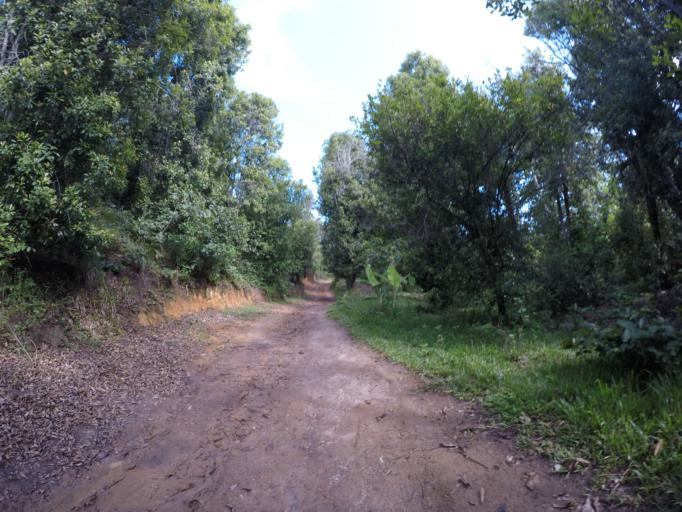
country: TZ
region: Pemba South
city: Mtambile
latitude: -5.3827
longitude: 39.7189
